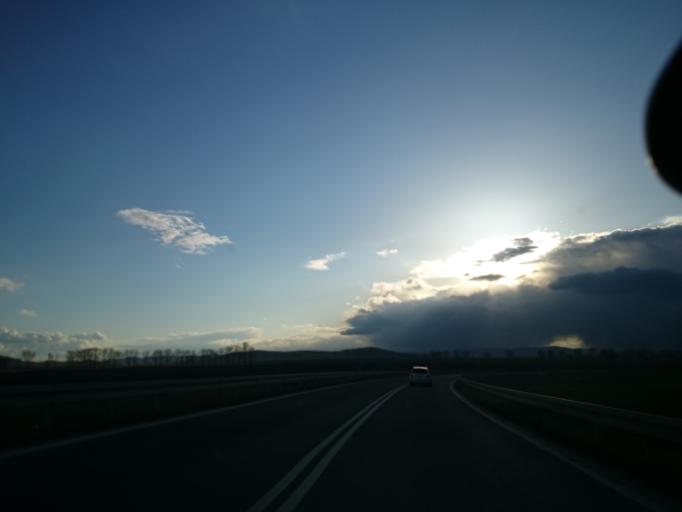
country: PL
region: Lower Silesian Voivodeship
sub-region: Powiat zabkowicki
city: Zabkowice Slaskie
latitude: 50.5707
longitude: 16.8306
